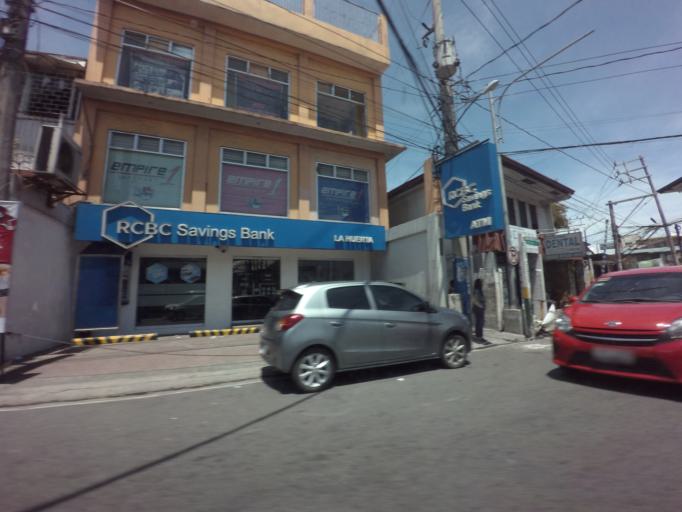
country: PH
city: Sambayanihan People's Village
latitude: 14.5014
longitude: 120.9925
